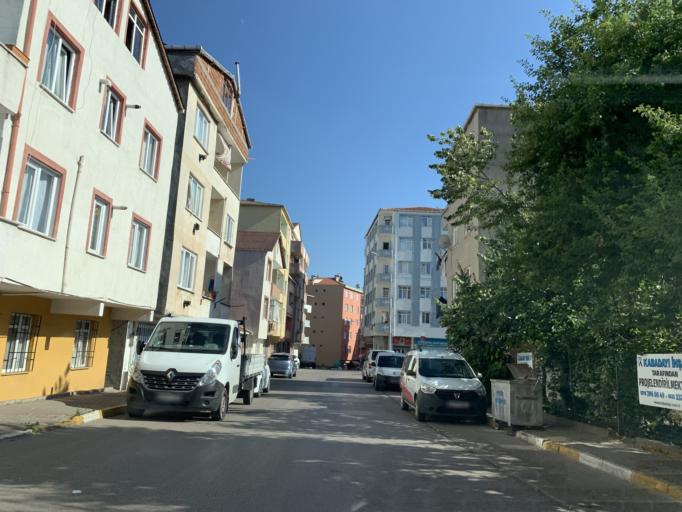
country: TR
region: Istanbul
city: Pendik
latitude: 40.8824
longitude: 29.2656
